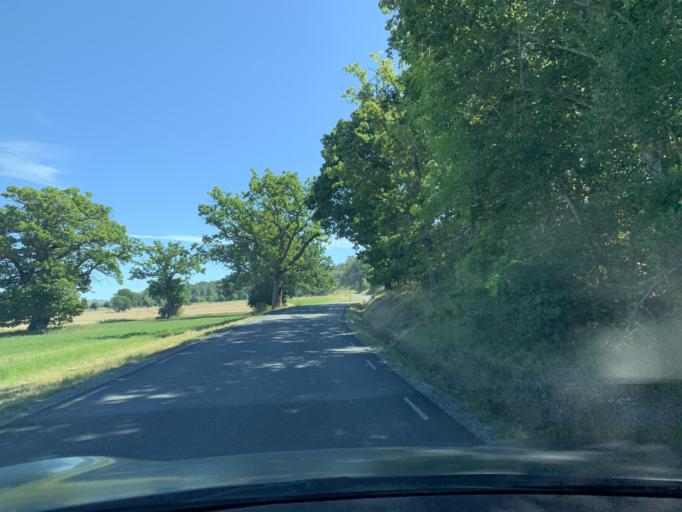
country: SE
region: Stockholm
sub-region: Botkyrka Kommun
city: Eriksberg
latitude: 59.2503
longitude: 17.7792
